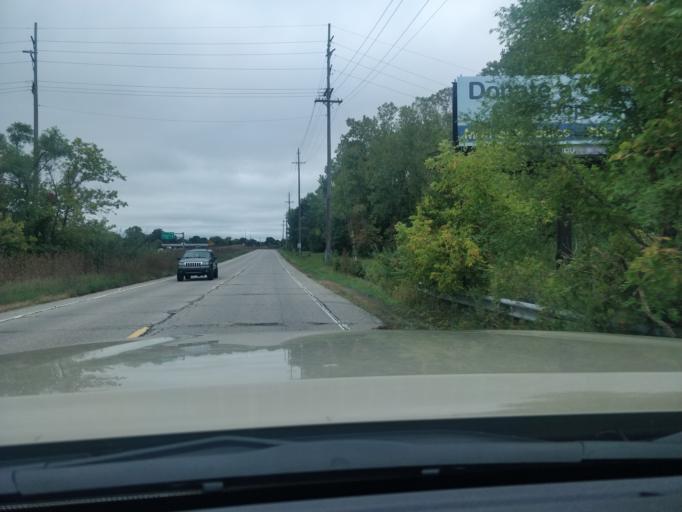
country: US
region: Michigan
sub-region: Wayne County
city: Romulus
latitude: 42.2210
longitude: -83.4310
